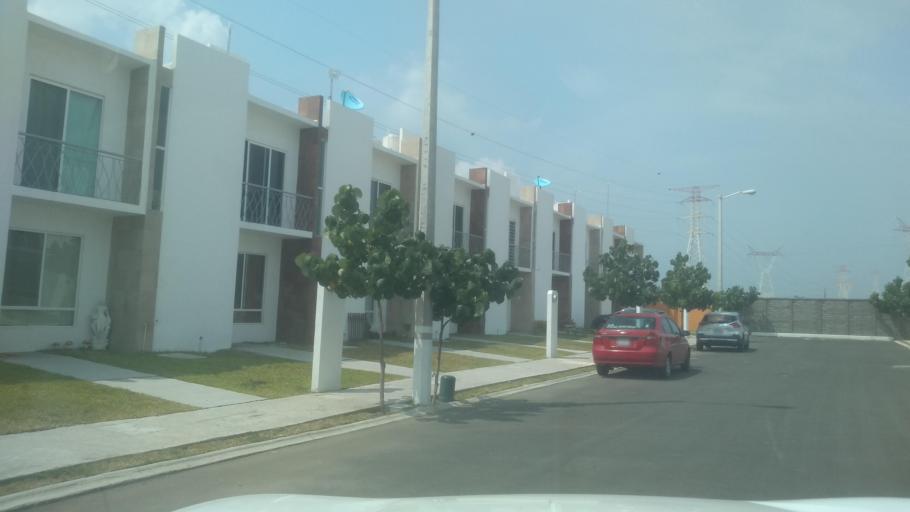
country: MX
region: Veracruz
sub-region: Veracruz
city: Las Amapolas
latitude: 19.1671
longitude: -96.1809
